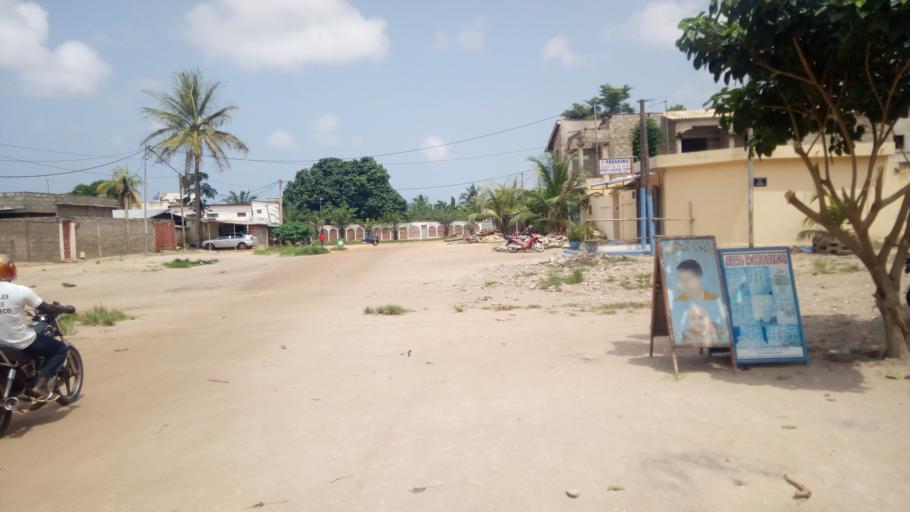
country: TG
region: Maritime
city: Lome
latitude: 6.1937
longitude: 1.1966
